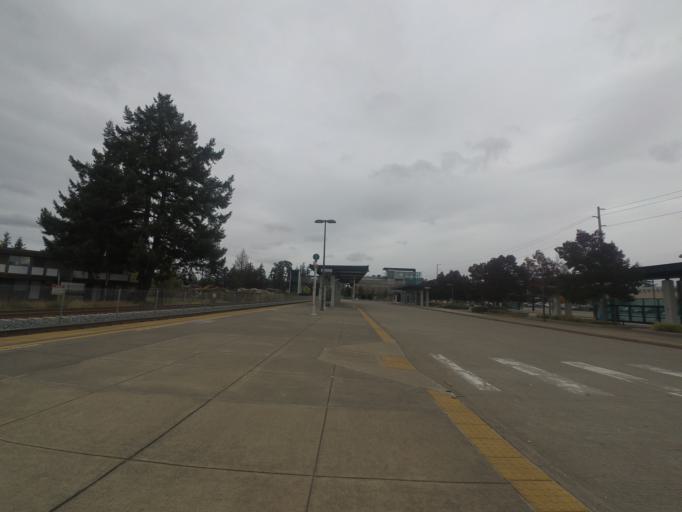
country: US
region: Washington
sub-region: Pierce County
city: McChord Air Force Base
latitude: 47.1527
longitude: -122.4998
